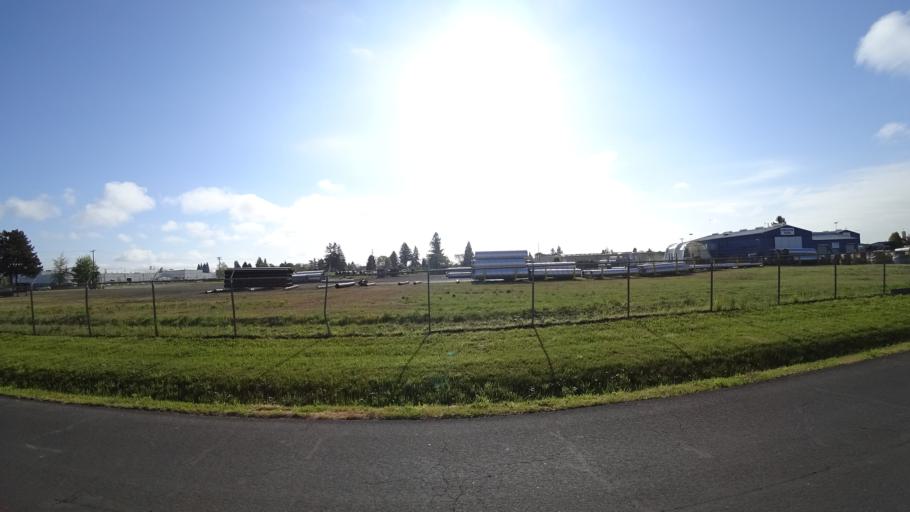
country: US
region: Oregon
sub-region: Washington County
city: Hillsboro
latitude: 45.5166
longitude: -123.0011
